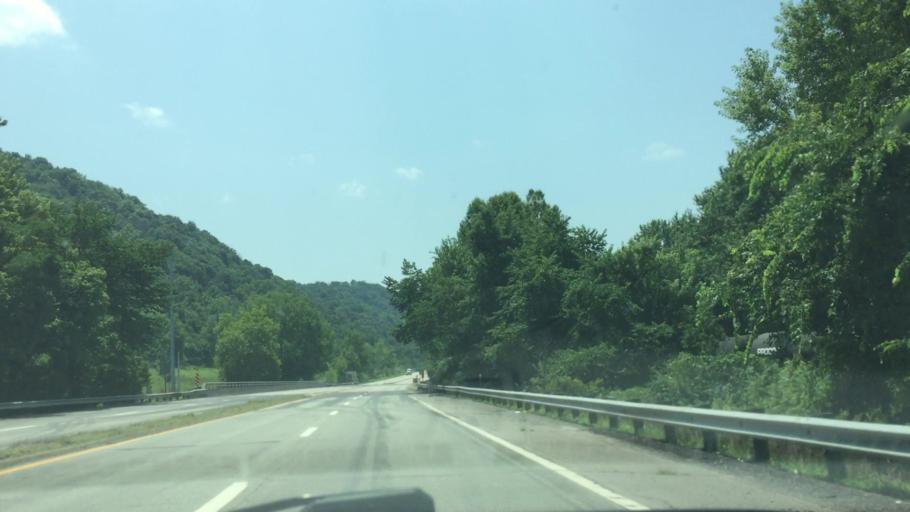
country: US
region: Ohio
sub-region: Belmont County
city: Powhatan Point
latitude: 39.8104
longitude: -80.8155
